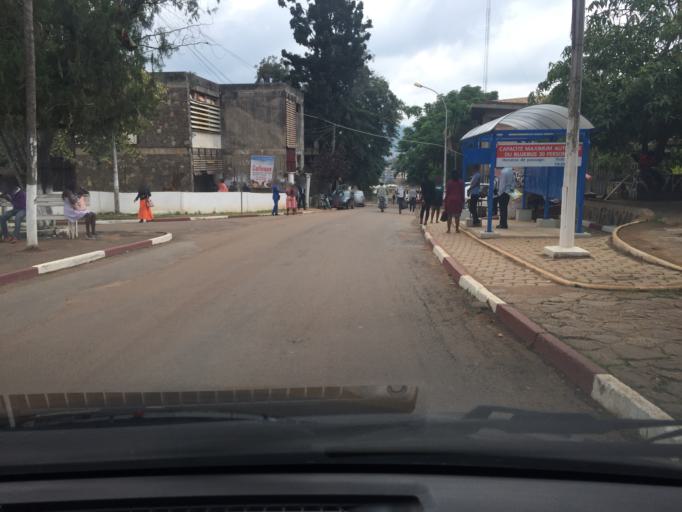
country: CM
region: Centre
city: Yaounde
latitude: 3.8581
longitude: 11.5020
